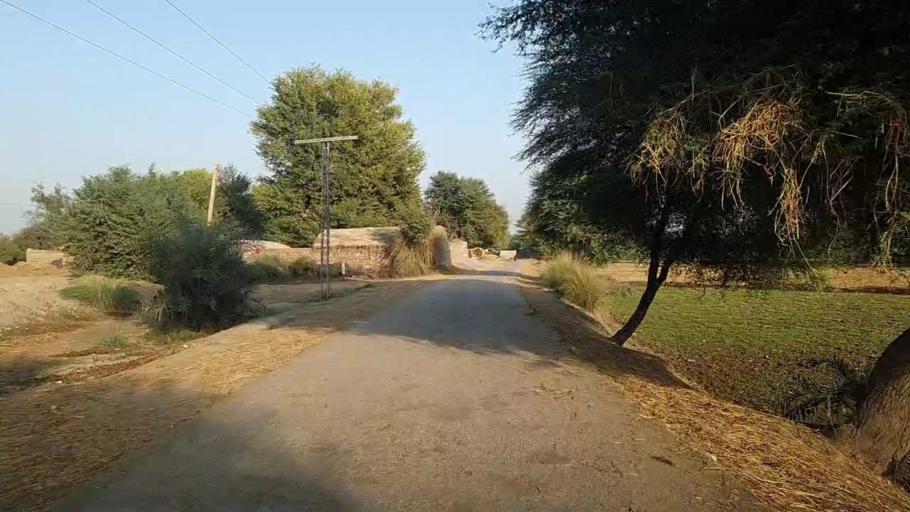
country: PK
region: Sindh
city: Kashmor
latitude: 28.4282
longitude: 69.4673
